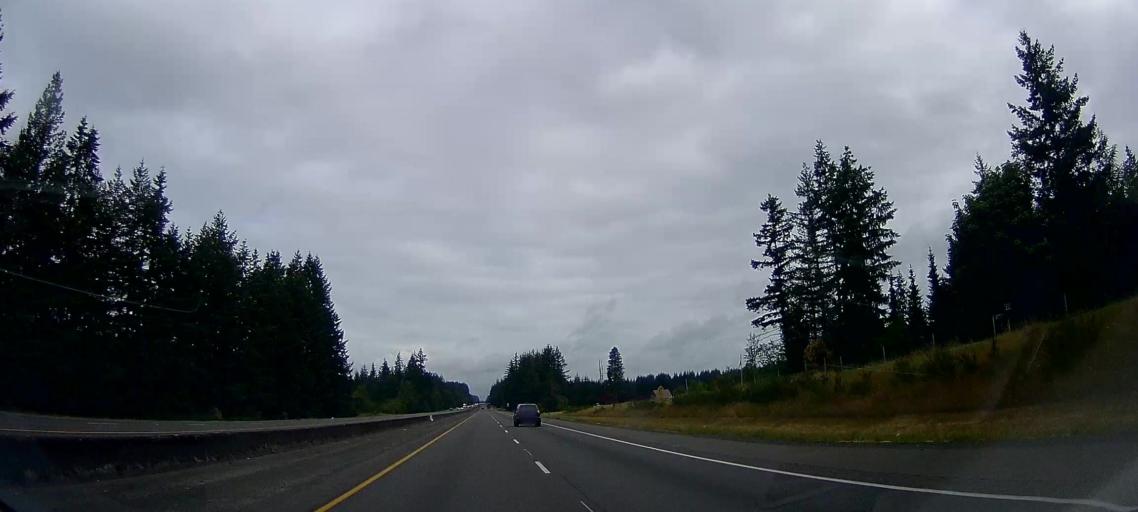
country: US
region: Washington
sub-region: Lewis County
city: Winlock
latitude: 46.5013
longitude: -122.8765
